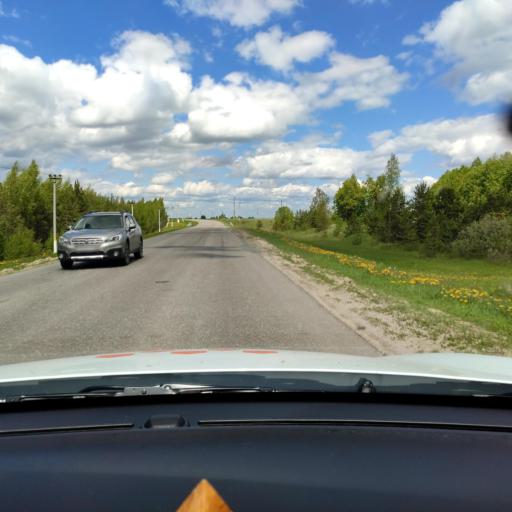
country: RU
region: Tatarstan
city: Verkhniy Uslon
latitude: 55.6174
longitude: 48.8790
